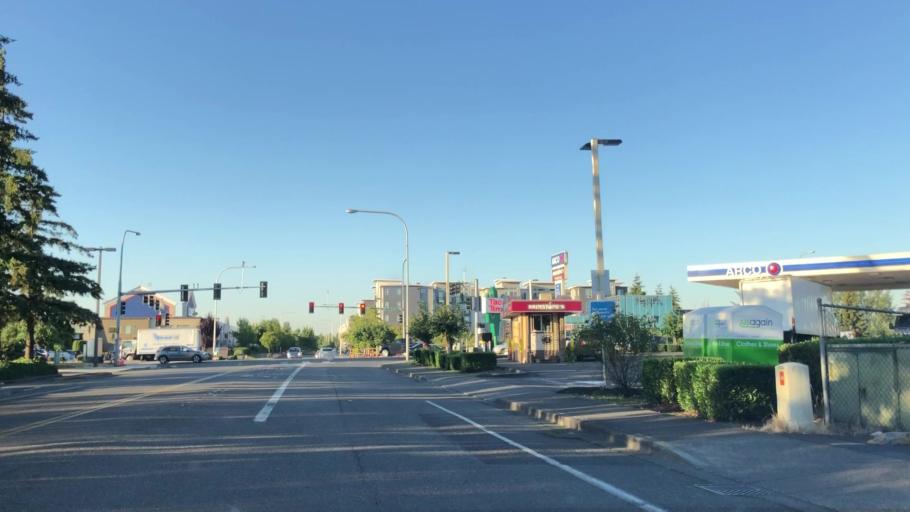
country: US
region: Washington
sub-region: King County
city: Auburn
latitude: 47.3217
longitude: -122.2288
